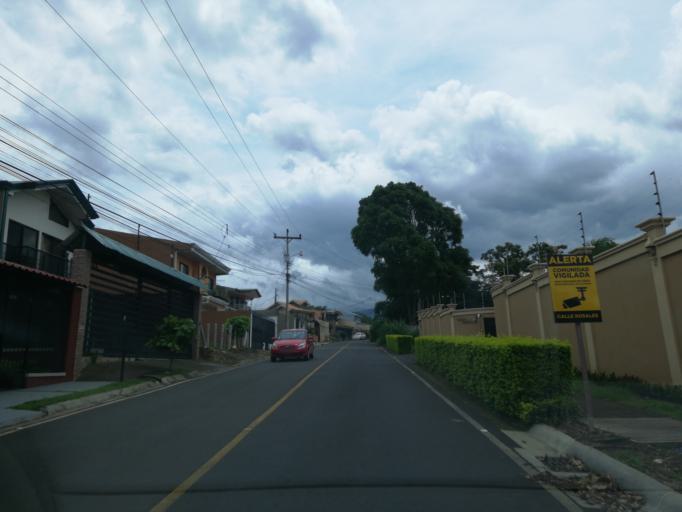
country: CR
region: Alajuela
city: Alajuela
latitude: 10.0284
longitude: -84.1964
